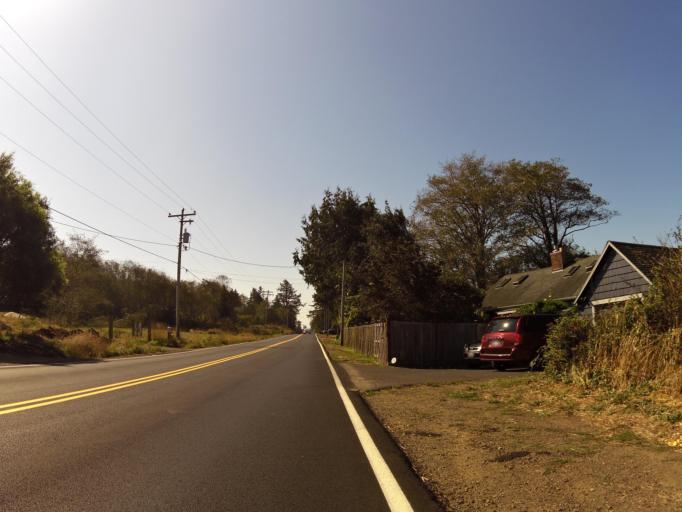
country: US
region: Oregon
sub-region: Tillamook County
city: Pacific City
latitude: 45.2674
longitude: -123.9482
